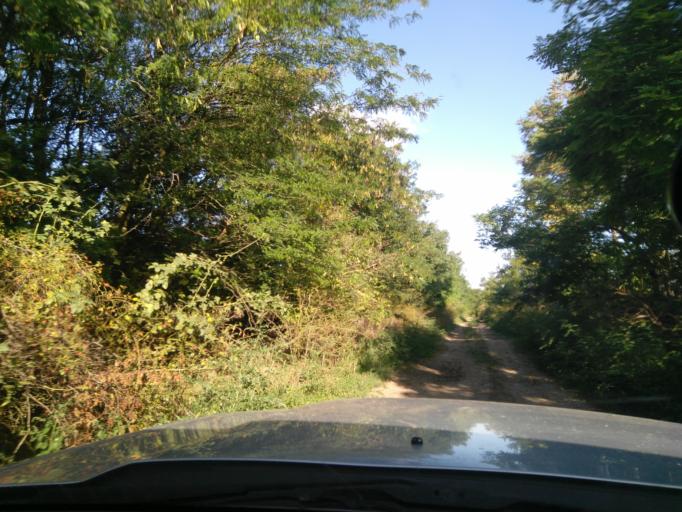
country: HU
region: Fejer
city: Kapolnasnyek
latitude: 47.2687
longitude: 18.7104
